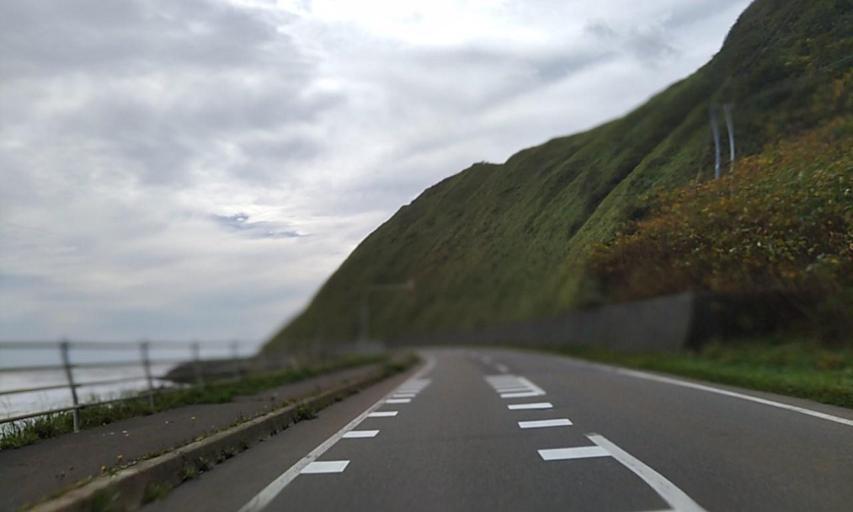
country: JP
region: Hokkaido
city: Kushiro
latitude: 42.7945
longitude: 143.8047
